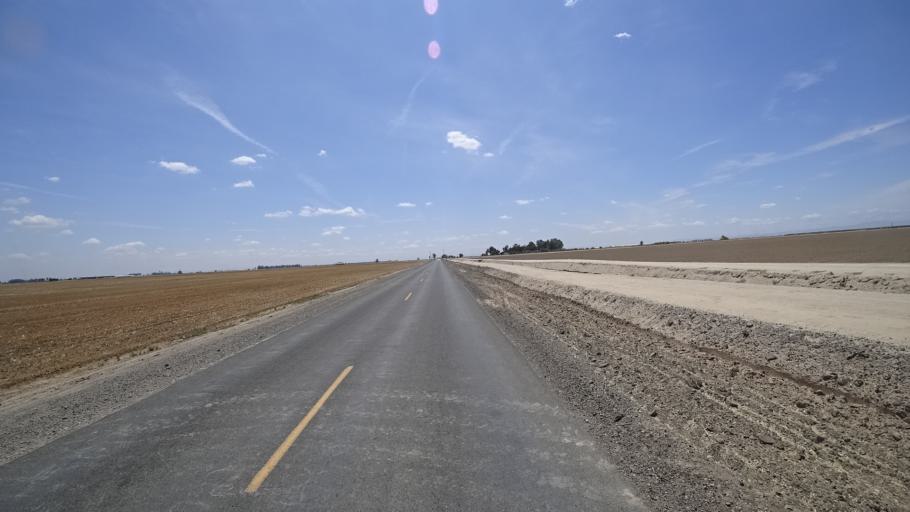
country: US
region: California
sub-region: Kings County
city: Home Garden
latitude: 36.2445
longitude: -119.6728
